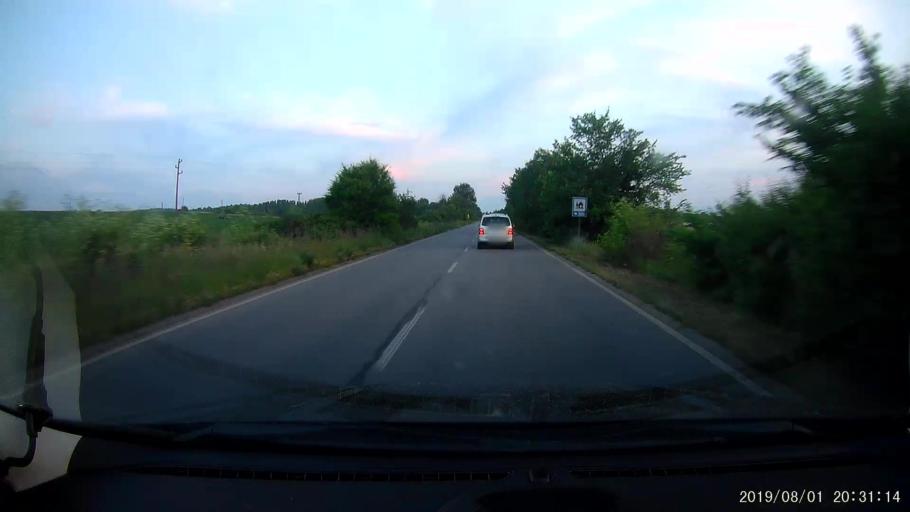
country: BG
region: Yambol
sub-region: Obshtina Elkhovo
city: Elkhovo
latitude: 42.1308
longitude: 26.5412
